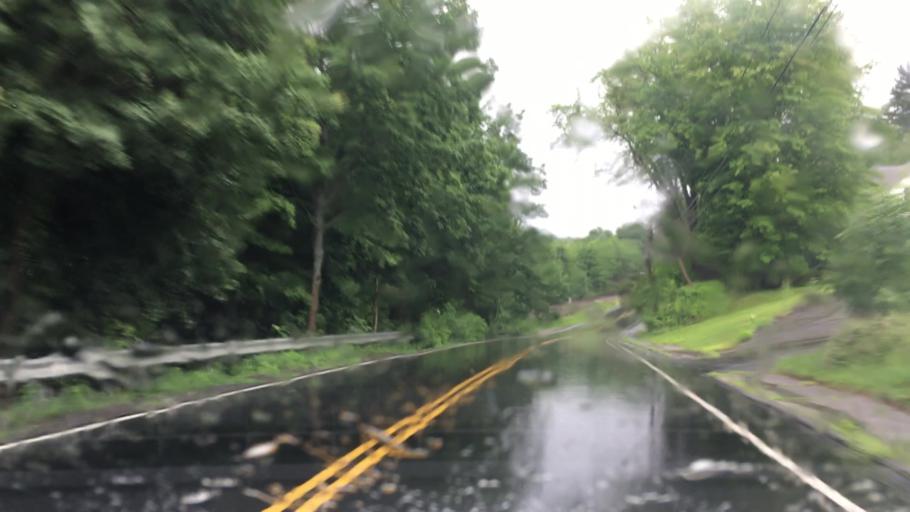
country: US
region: Maine
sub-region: Kennebec County
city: Randolph
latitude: 44.2252
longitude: -69.7663
